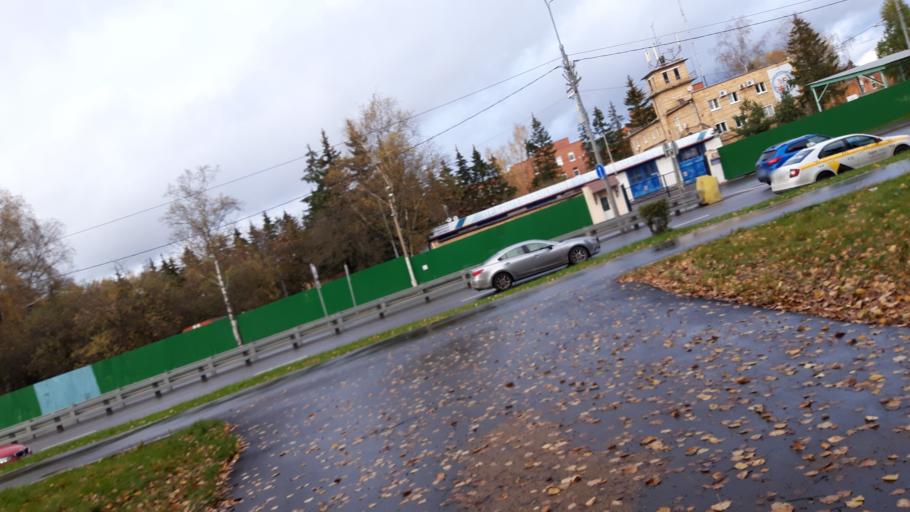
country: RU
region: Moscow
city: Zelenograd
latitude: 55.9808
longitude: 37.2026
